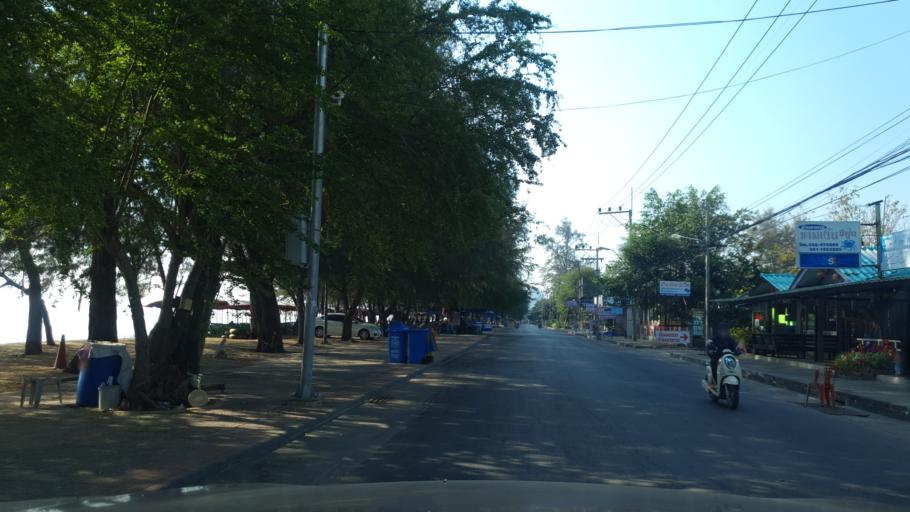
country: TH
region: Phetchaburi
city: Cha-am
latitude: 12.7809
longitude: 99.9787
